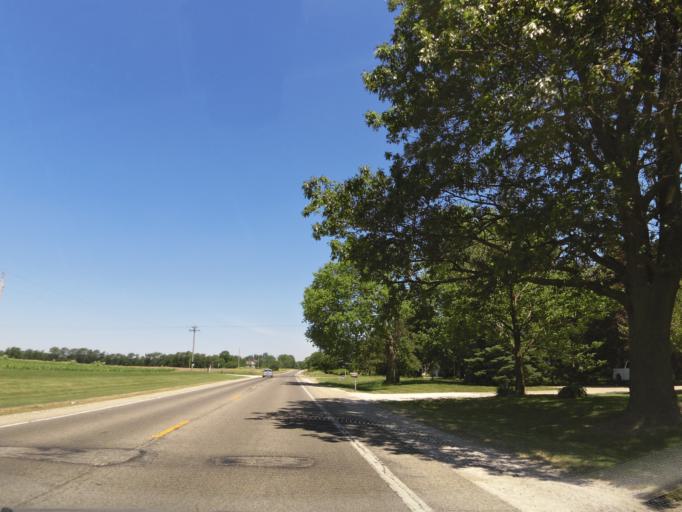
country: US
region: Illinois
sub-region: Vermilion County
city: Rossville
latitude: 40.4142
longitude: -87.6840
